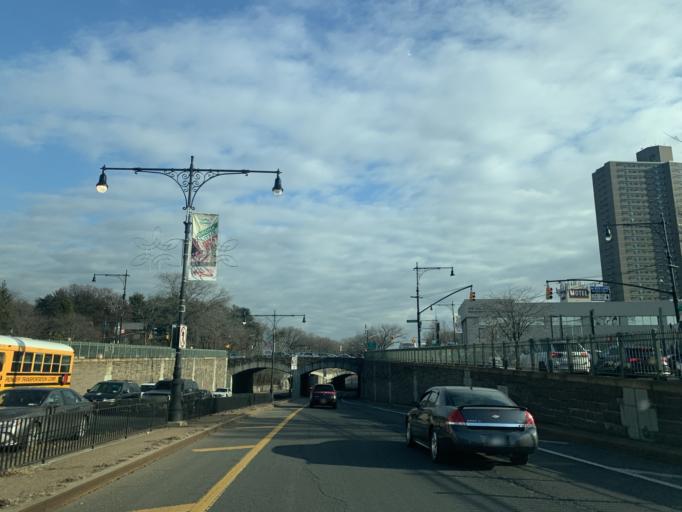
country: US
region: New York
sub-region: Bronx
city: The Bronx
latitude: 40.8572
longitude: -73.8816
